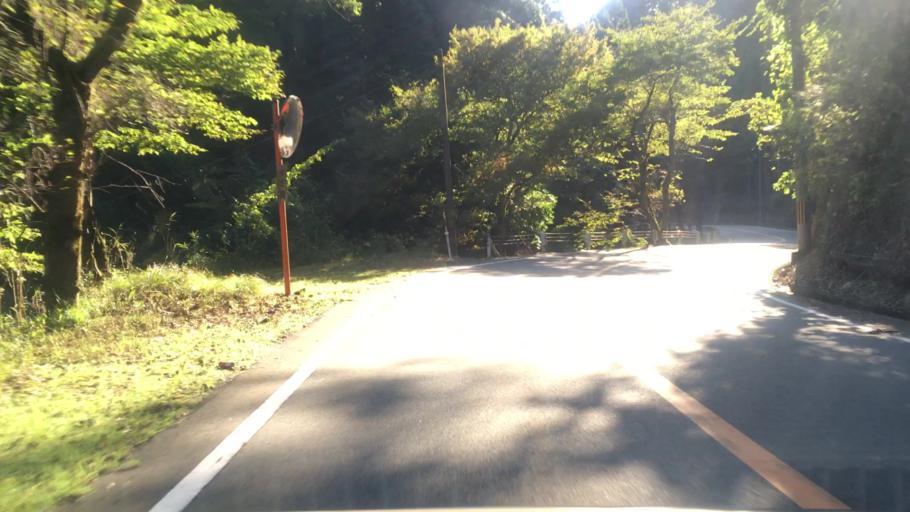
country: JP
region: Hyogo
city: Toyooka
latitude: 35.6184
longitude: 134.8604
